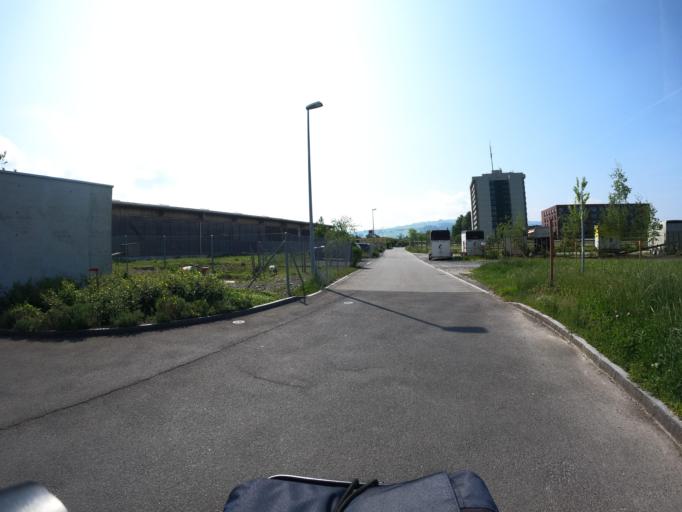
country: CH
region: Zug
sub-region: Zug
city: Baar
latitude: 47.1970
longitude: 8.5181
